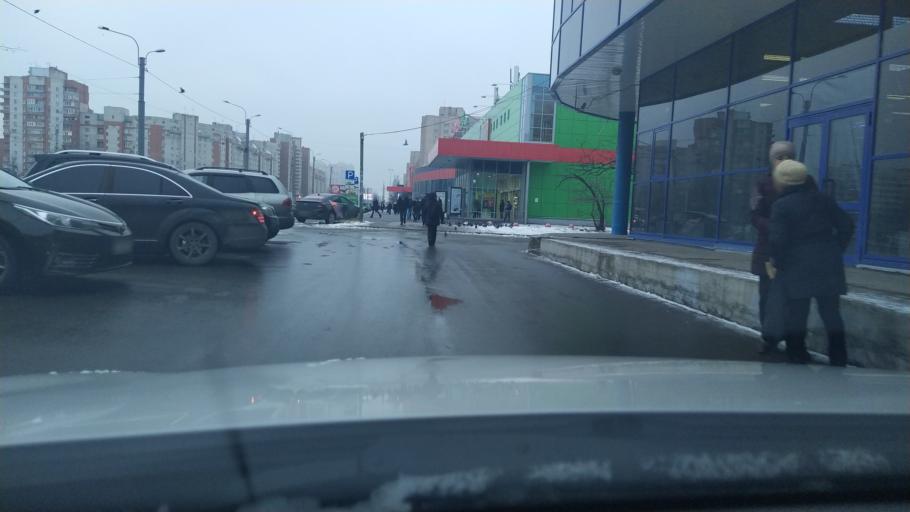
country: RU
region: St.-Petersburg
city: Grazhdanka
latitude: 60.0418
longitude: 30.3910
